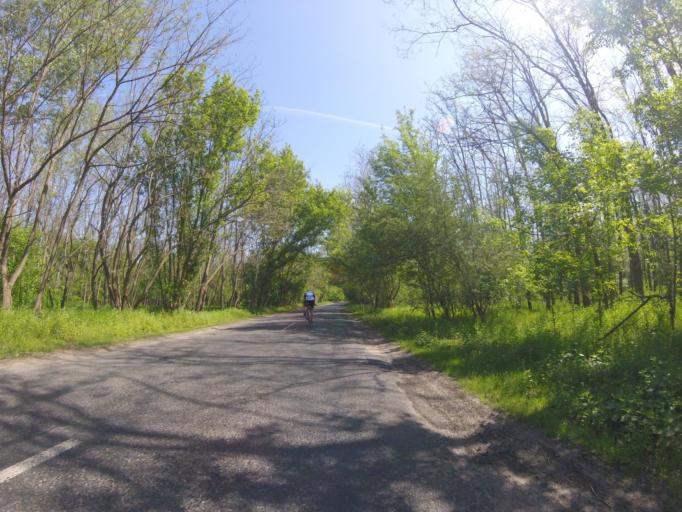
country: HU
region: Pest
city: Hernad
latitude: 47.1613
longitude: 19.4893
